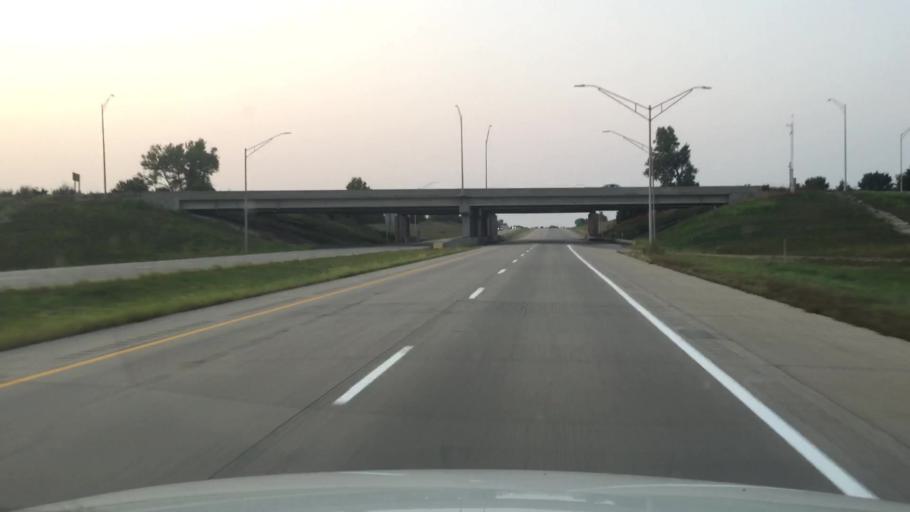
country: US
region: Iowa
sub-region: Clarke County
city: Osceola
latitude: 41.0256
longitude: -93.7942
